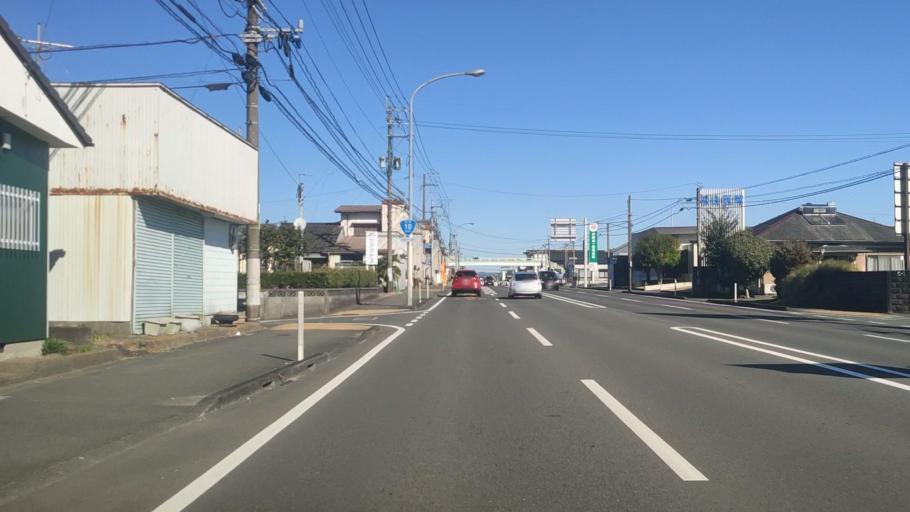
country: JP
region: Miyazaki
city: Miyakonojo
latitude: 31.7411
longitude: 131.0726
